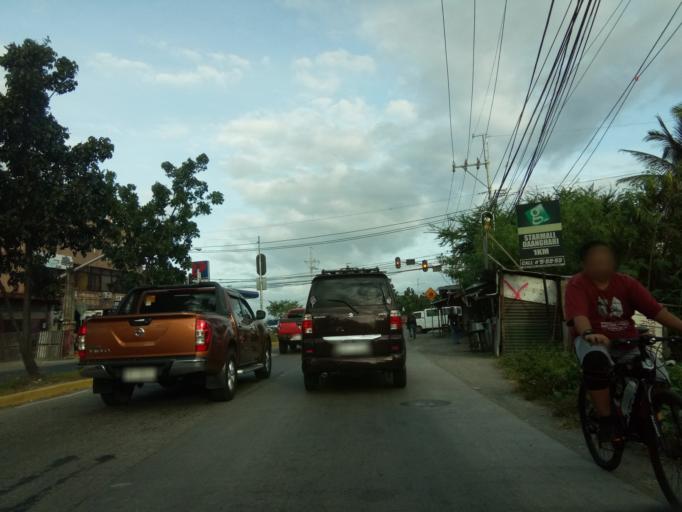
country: PH
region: Calabarzon
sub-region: Province of Cavite
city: Imus
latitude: 14.3887
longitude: 120.9672
